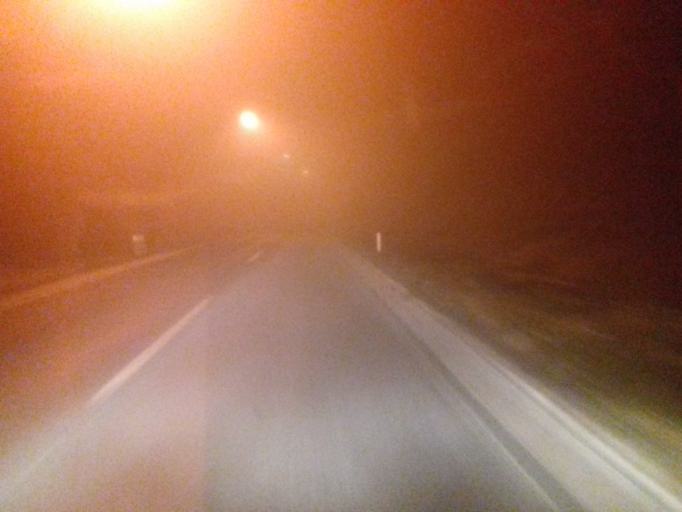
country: BA
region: Federation of Bosnia and Herzegovina
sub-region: Kanton Sarajevo
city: Sarajevo
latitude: 43.7837
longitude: 18.3606
